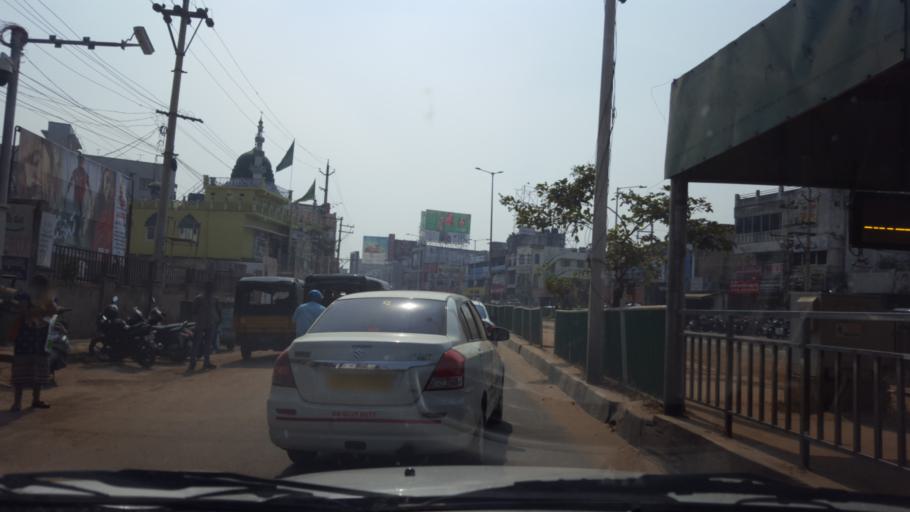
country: IN
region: Andhra Pradesh
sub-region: Vishakhapatnam
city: Vepagunta
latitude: 17.7493
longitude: 83.2189
